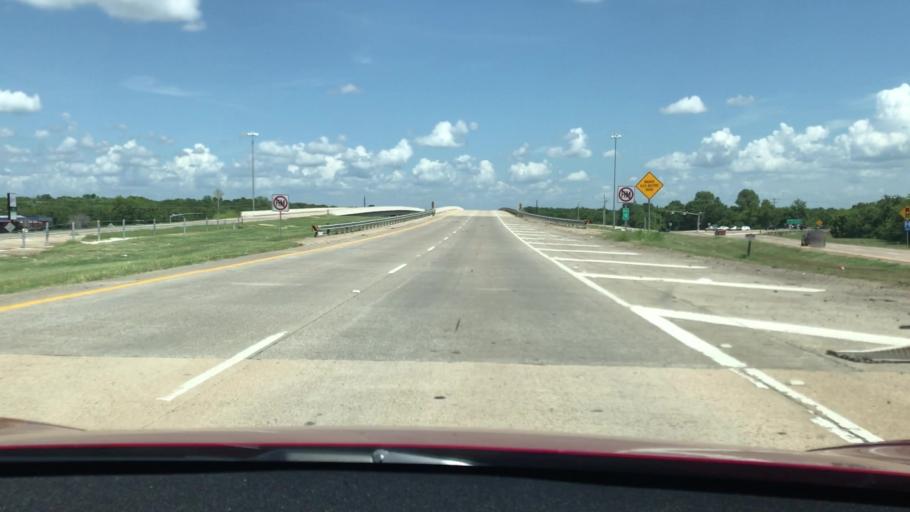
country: US
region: Louisiana
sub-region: Bossier Parish
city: Bossier City
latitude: 32.4124
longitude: -93.7278
